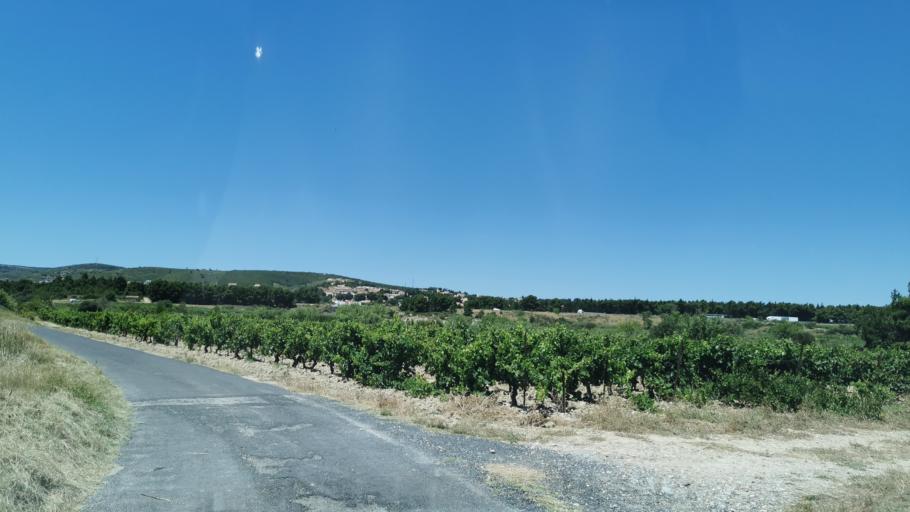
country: FR
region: Languedoc-Roussillon
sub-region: Departement de l'Aude
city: Peyriac-de-Mer
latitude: 43.1351
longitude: 2.9787
